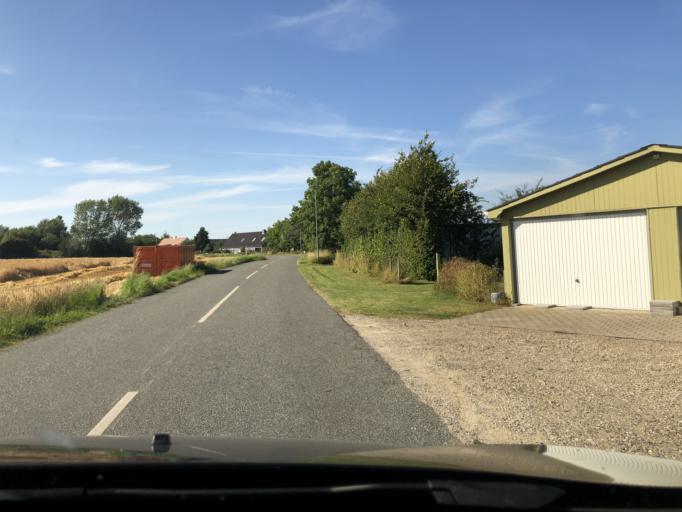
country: DK
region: South Denmark
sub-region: AEro Kommune
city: Marstal
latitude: 54.8644
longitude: 10.5034
